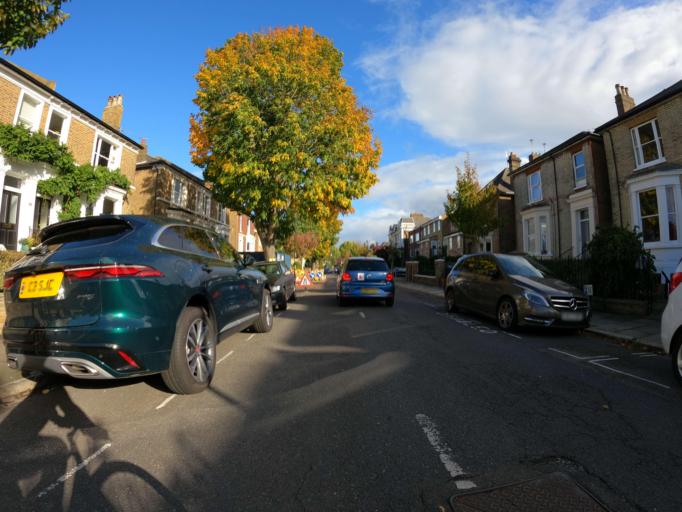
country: GB
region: England
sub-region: Greater London
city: Ealing
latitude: 51.5049
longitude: -0.3011
